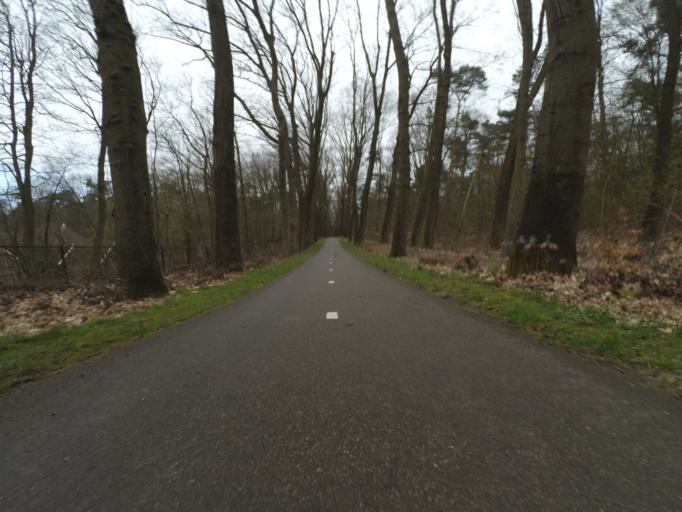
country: NL
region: Gelderland
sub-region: Gemeente Arnhem
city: Burgemeesterswijk
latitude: 52.0128
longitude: 5.9174
